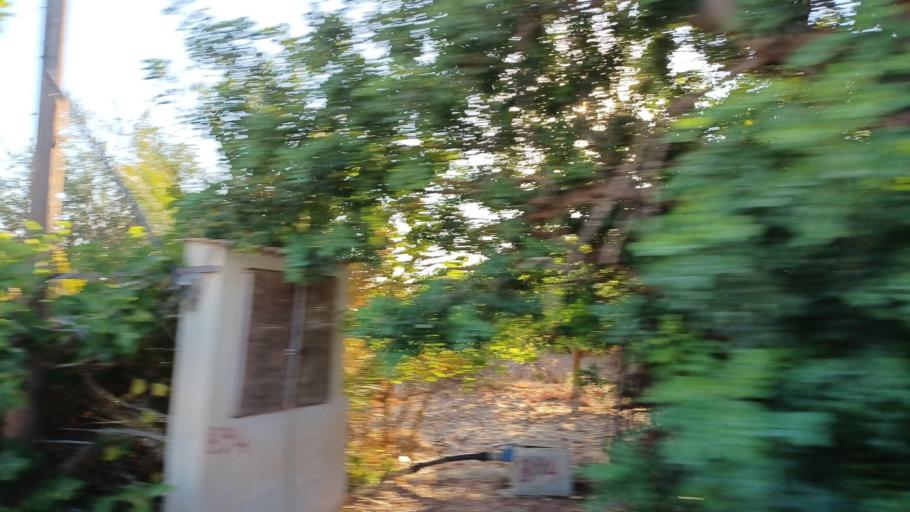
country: CY
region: Pafos
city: Polis
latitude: 35.0315
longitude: 32.3898
